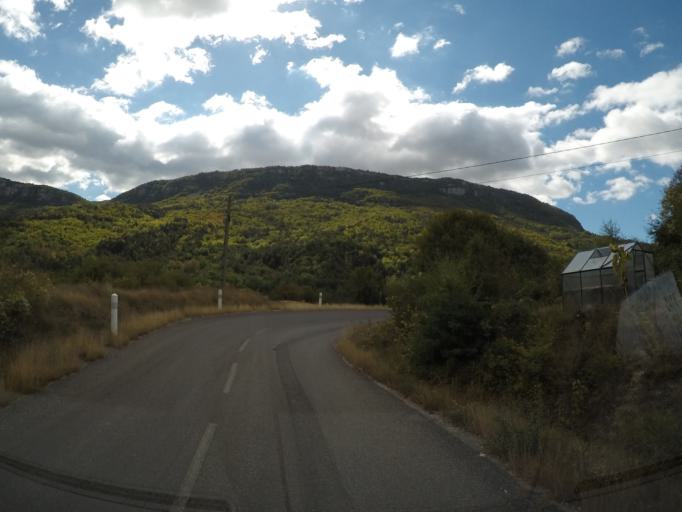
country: FR
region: Provence-Alpes-Cote d'Azur
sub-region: Departement des Hautes-Alpes
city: Laragne-Monteglin
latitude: 44.1777
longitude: 5.6640
